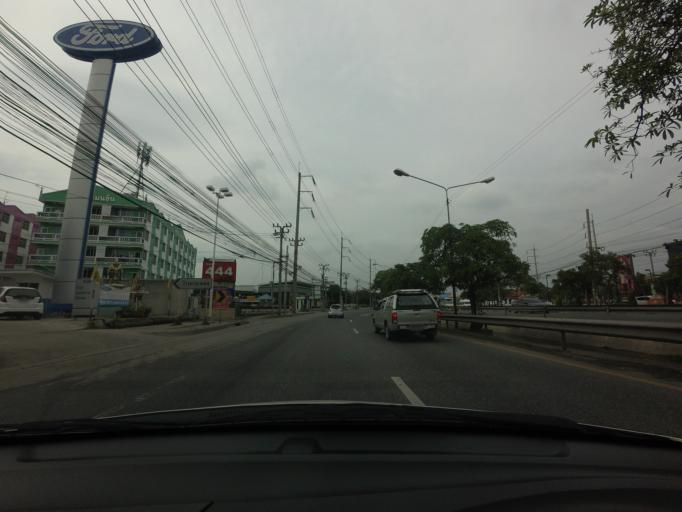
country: TH
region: Samut Prakan
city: Samut Prakan
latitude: 13.5387
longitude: 100.6218
